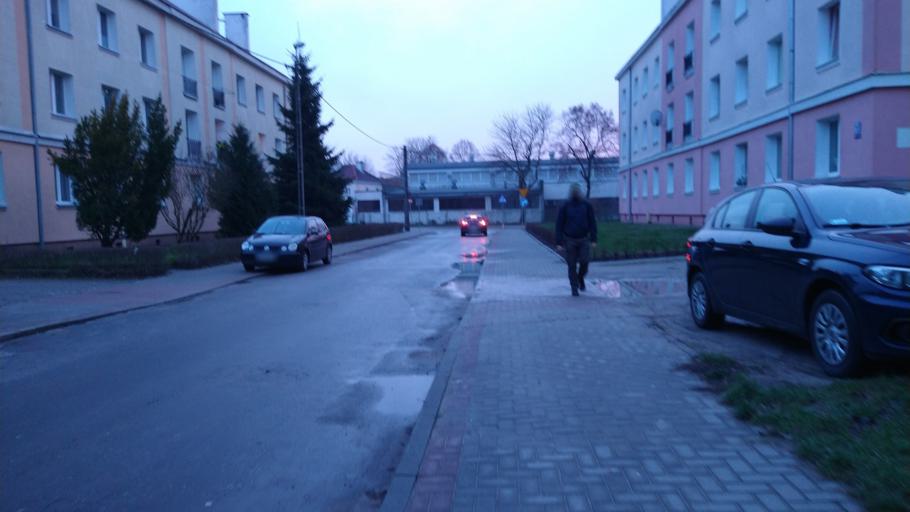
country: PL
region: Warmian-Masurian Voivodeship
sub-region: Powiat olsztynski
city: Olsztyn
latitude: 53.7879
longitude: 20.4959
